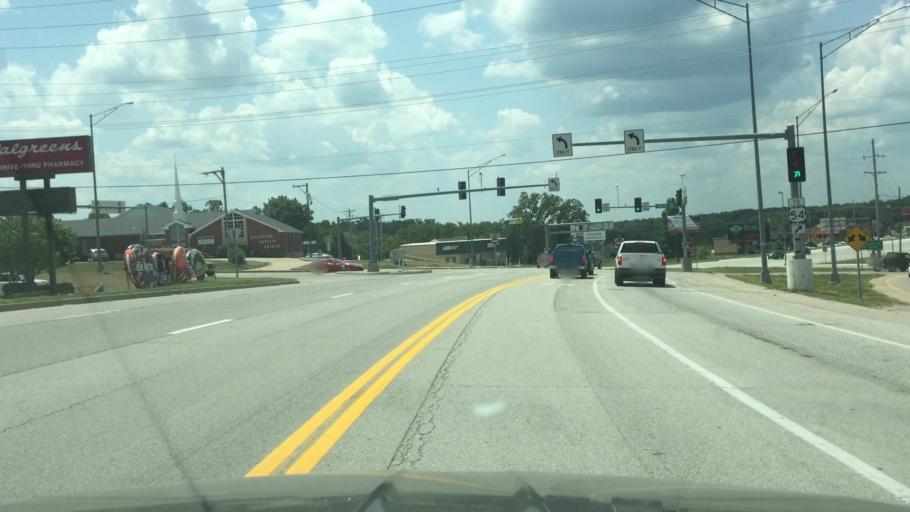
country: US
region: Missouri
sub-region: Miller County
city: Lake Ozark
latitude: 38.1575
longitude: -92.6050
